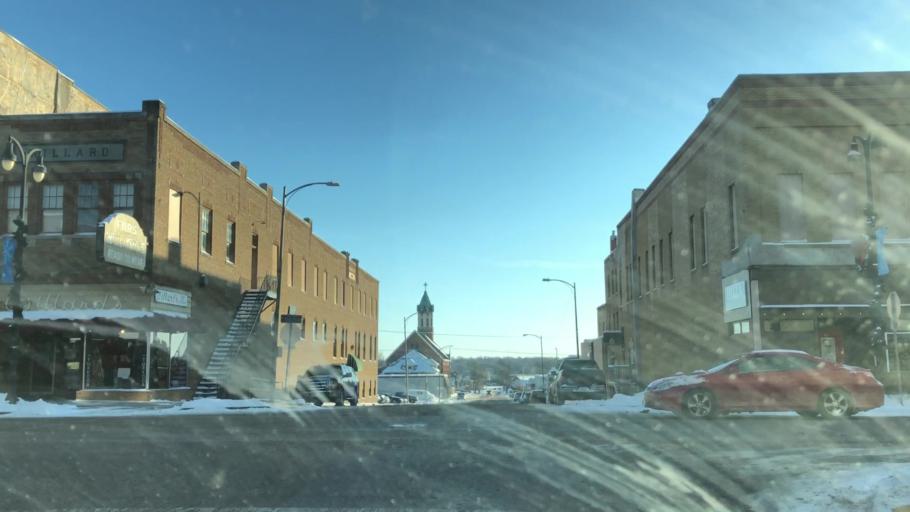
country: US
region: Iowa
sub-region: Marshall County
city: Marshalltown
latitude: 42.0493
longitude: -92.9147
